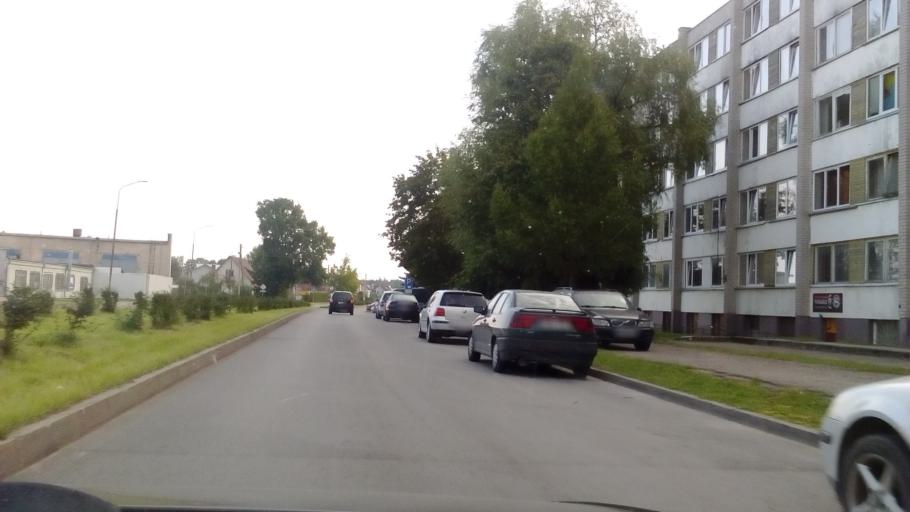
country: LT
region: Alytaus apskritis
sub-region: Alytus
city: Alytus
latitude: 54.3841
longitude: 24.0562
